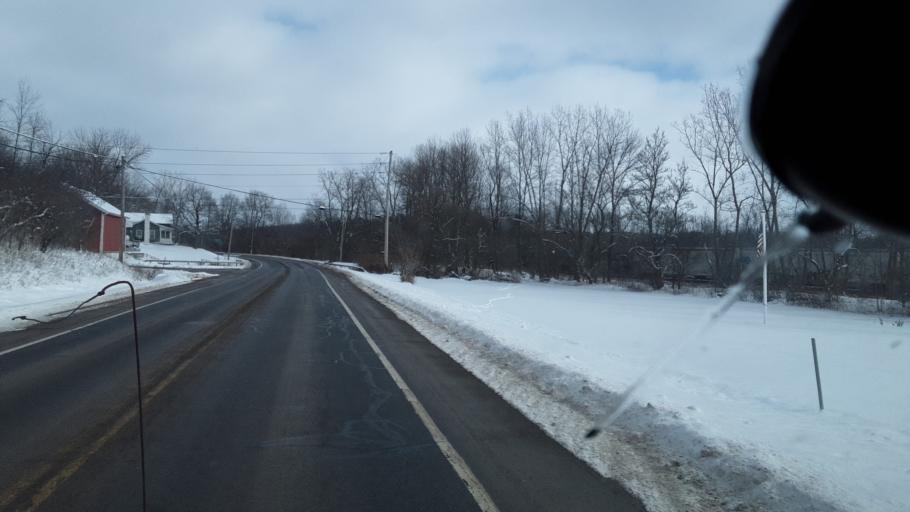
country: US
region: New York
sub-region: Wayne County
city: Newark
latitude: 43.0549
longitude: -77.0705
